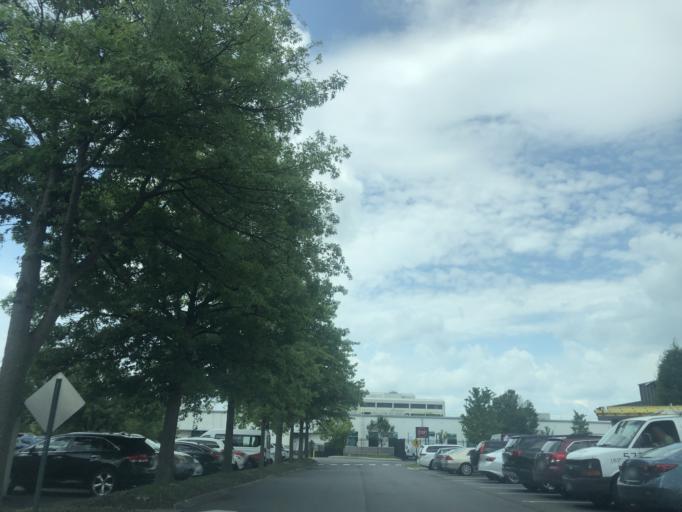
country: US
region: Tennessee
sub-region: Davidson County
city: Nashville
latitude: 36.1944
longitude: -86.7892
